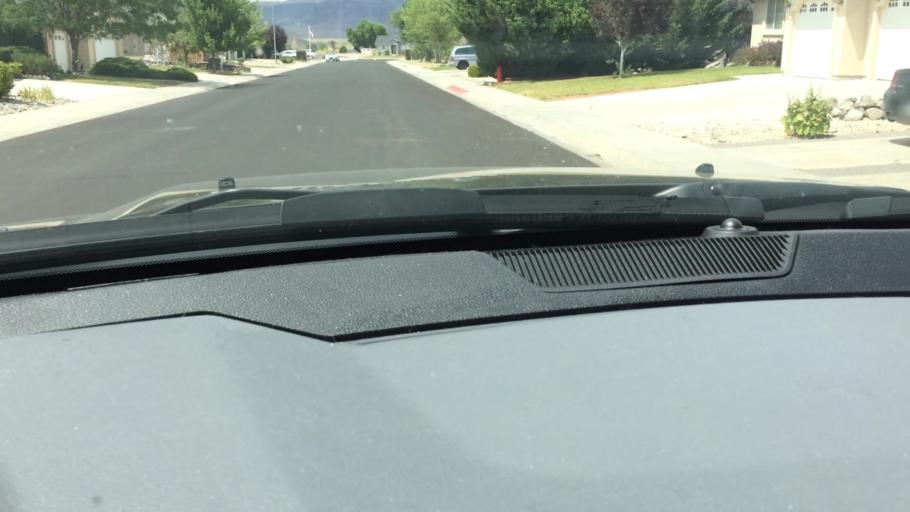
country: US
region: Nevada
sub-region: Lyon County
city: Fernley
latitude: 39.5901
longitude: -119.1544
